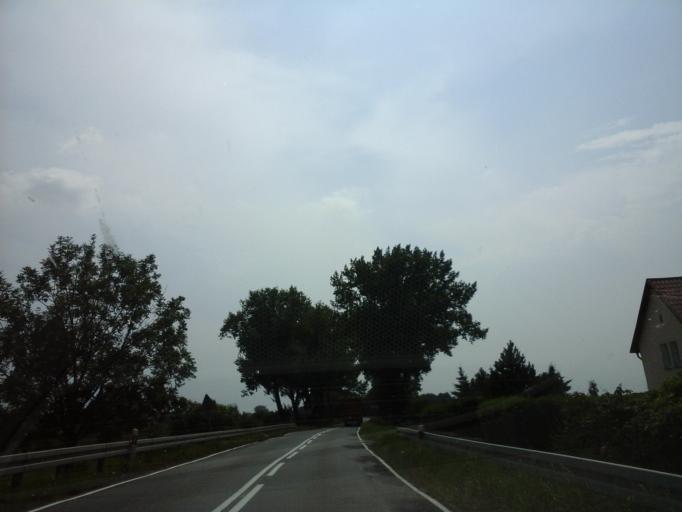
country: PL
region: Lower Silesian Voivodeship
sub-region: Powiat wroclawski
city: Zorawina
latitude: 50.9406
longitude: 17.0704
